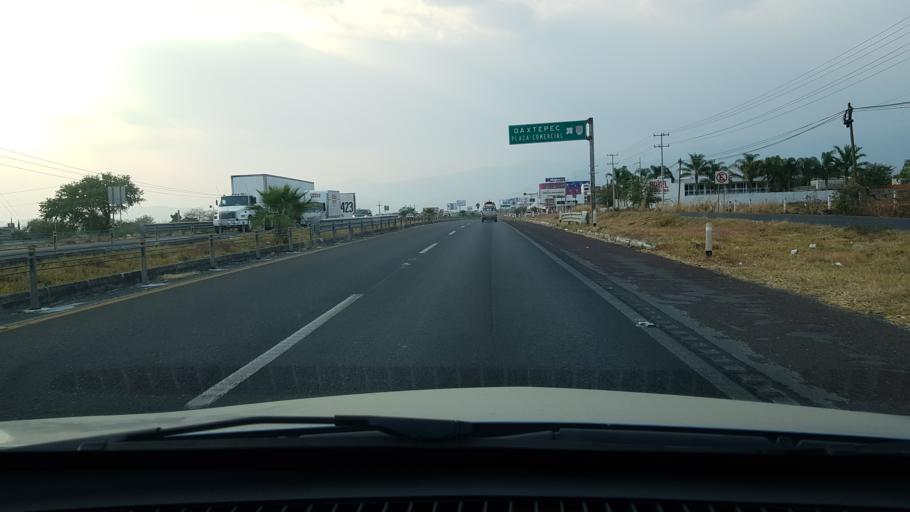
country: MX
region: Morelos
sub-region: Cuautla
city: Tierra Larga (Campo Nuevo)
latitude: 18.8619
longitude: -98.9468
